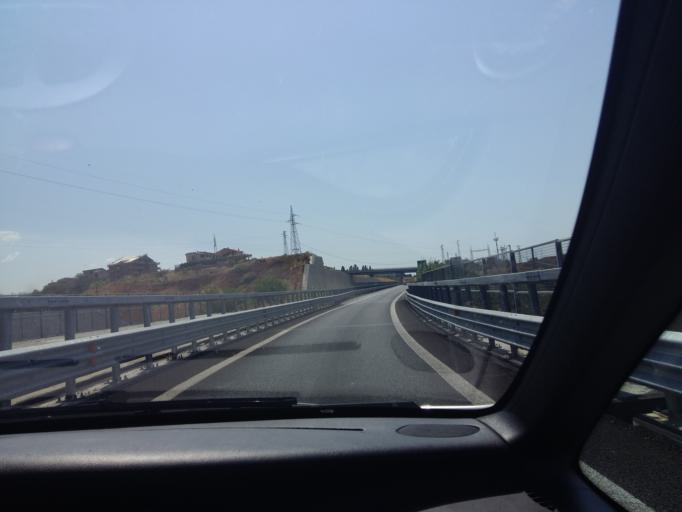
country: IT
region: Calabria
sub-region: Provincia di Reggio Calabria
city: Campo Calabro
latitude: 38.2216
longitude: 15.6475
